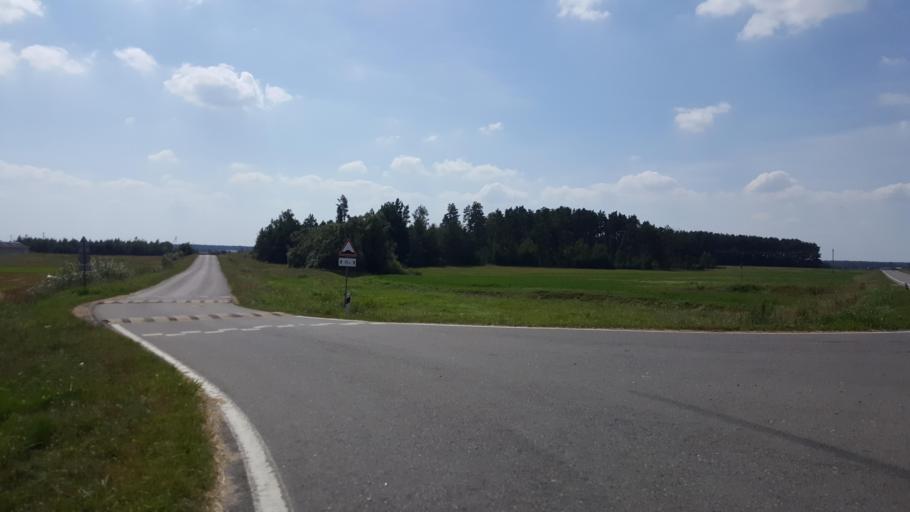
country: PL
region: Podlasie
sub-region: Powiat hajnowski
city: Czeremcha
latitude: 52.5445
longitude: 23.5446
